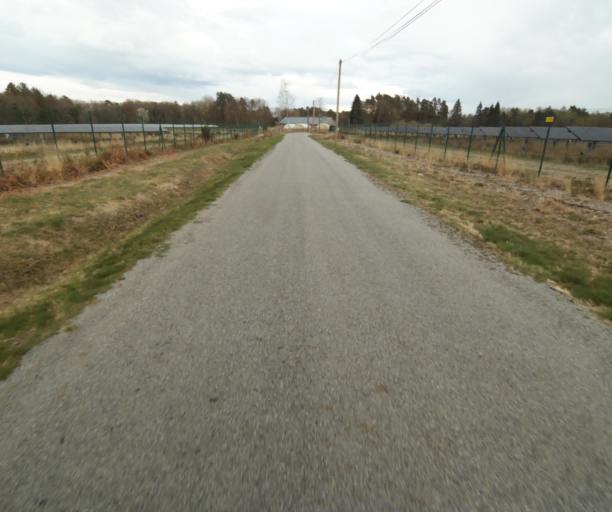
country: FR
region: Limousin
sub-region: Departement de la Correze
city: Saint-Privat
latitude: 45.2091
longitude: 2.0079
